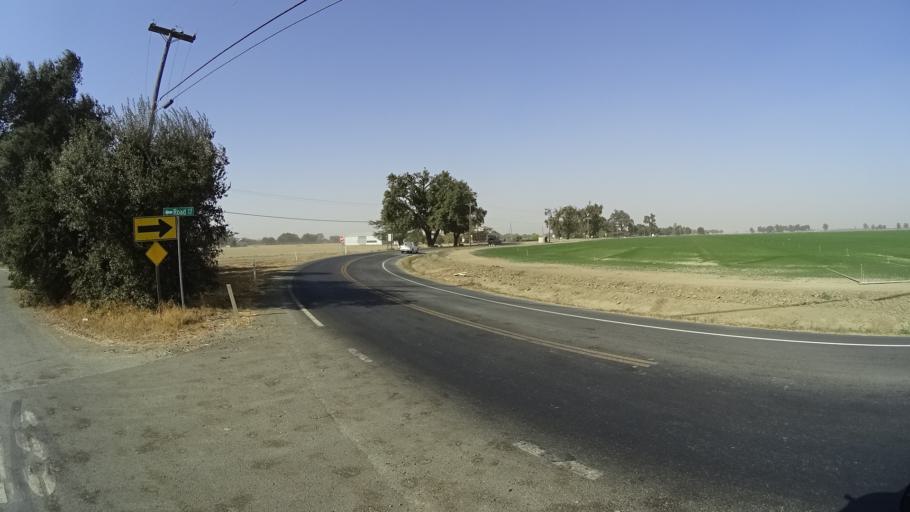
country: US
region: California
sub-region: Yolo County
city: Woodland
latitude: 38.7353
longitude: -121.7752
